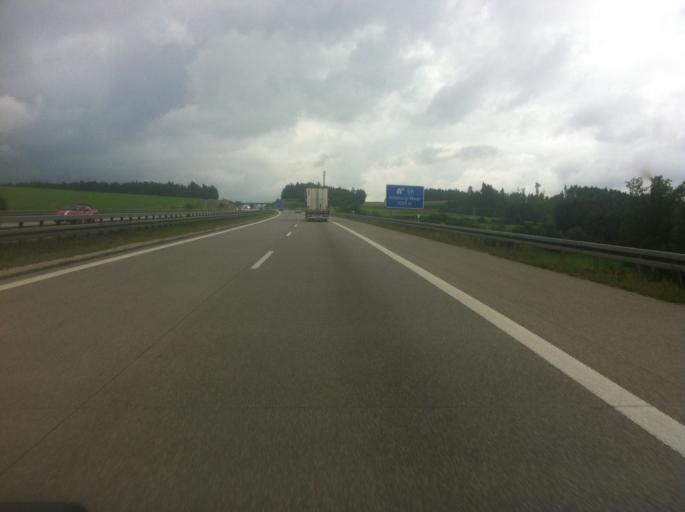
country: DE
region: Bavaria
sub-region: Upper Palatinate
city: Pfreimd
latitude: 49.4786
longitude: 12.1350
